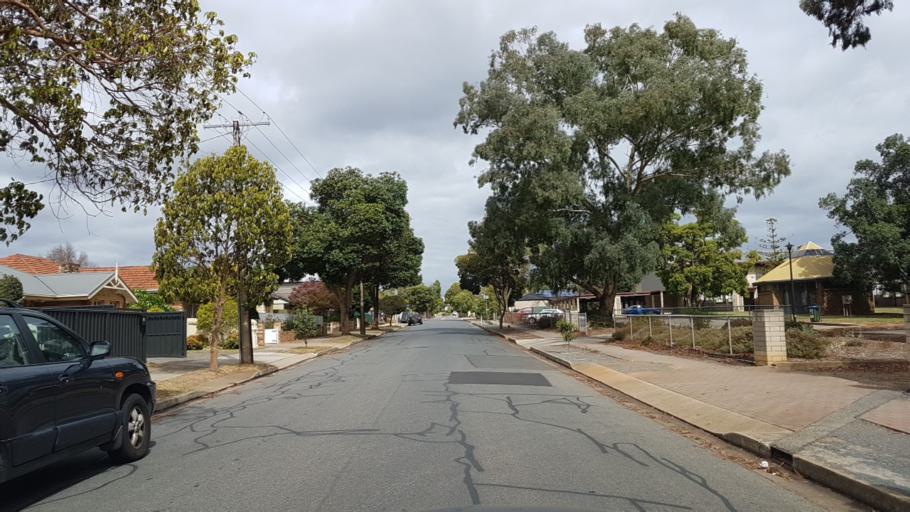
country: AU
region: South Australia
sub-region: Marion
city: Clovelly Park
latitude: -35.0008
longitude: 138.5743
